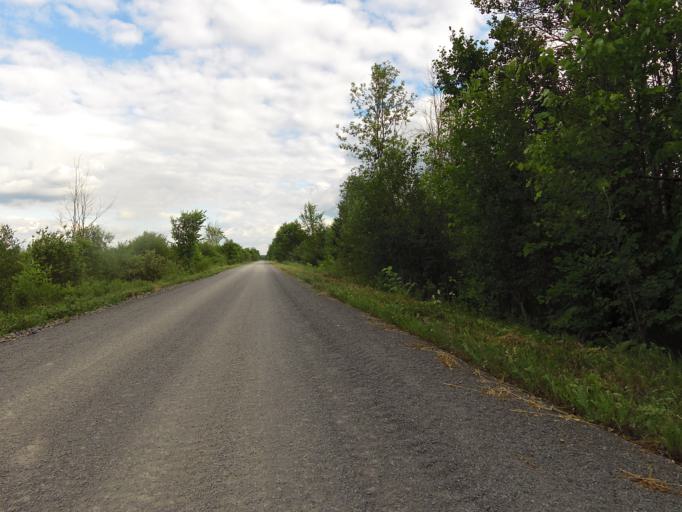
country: CA
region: Ontario
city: Arnprior
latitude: 45.2939
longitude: -76.2589
